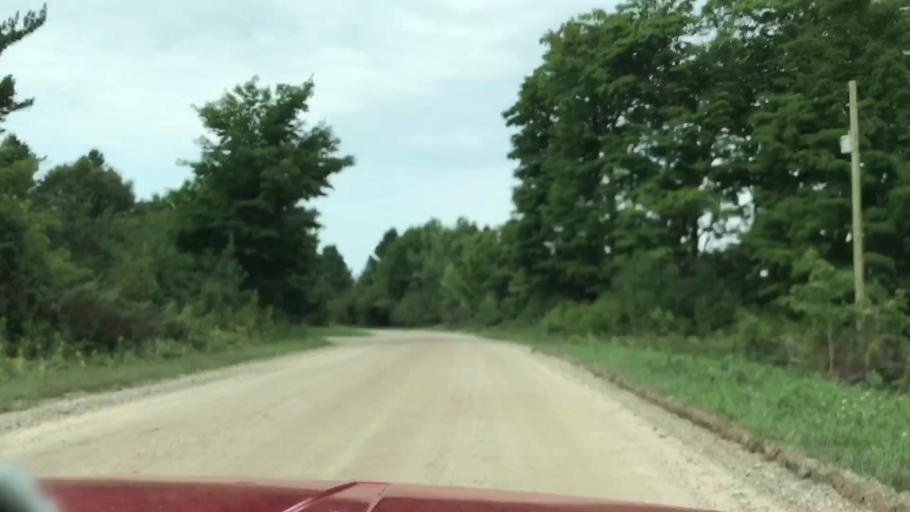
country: US
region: Michigan
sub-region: Charlevoix County
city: Charlevoix
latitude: 45.7282
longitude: -85.5463
